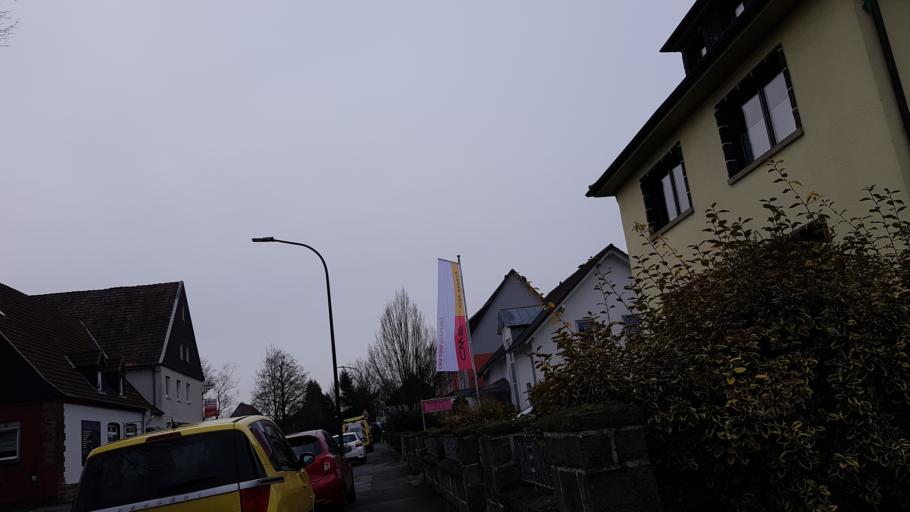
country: DE
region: North Rhine-Westphalia
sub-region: Regierungsbezirk Arnsberg
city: Bonen
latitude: 51.6393
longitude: 7.7836
